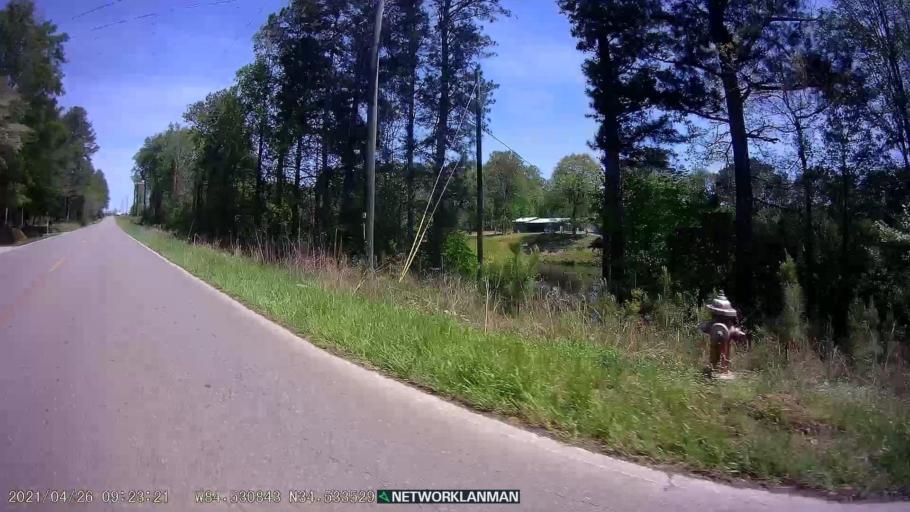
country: US
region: Georgia
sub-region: Pickens County
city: Jasper
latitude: 34.5338
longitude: -84.5311
